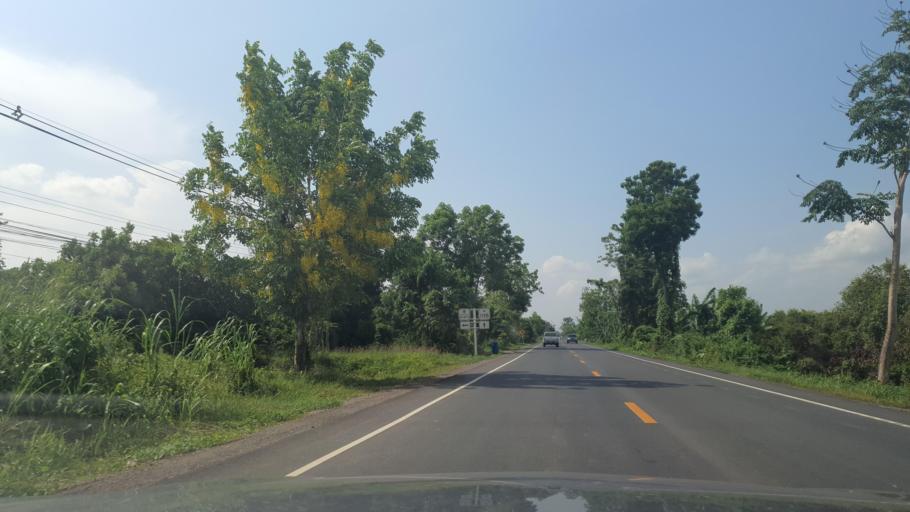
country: TH
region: Sukhothai
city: Si Samrong
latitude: 17.2101
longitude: 99.8494
